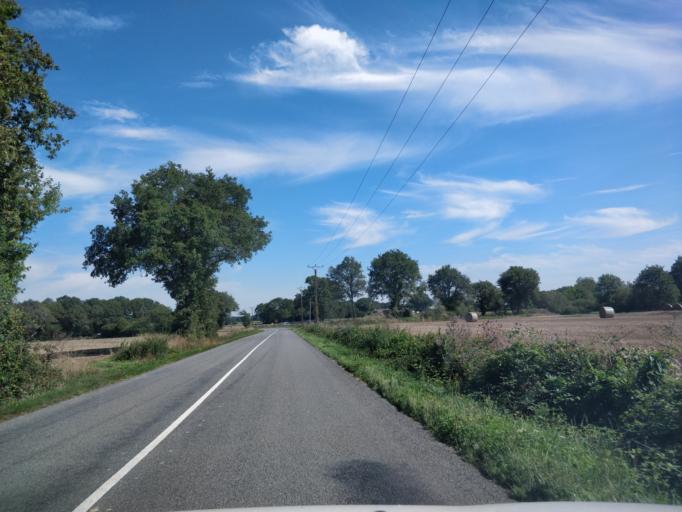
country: FR
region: Pays de la Loire
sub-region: Departement de la Loire-Atlantique
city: Conquereuil
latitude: 47.6592
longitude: -1.7814
